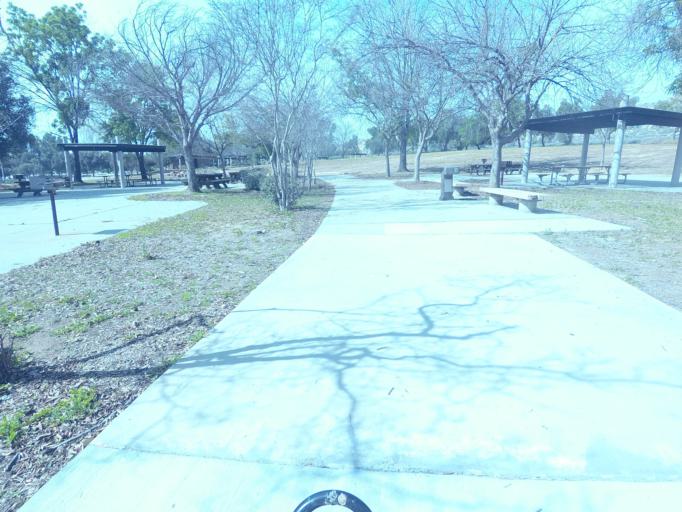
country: US
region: California
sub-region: Riverside County
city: Lakeview
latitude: 33.8650
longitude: -117.1896
